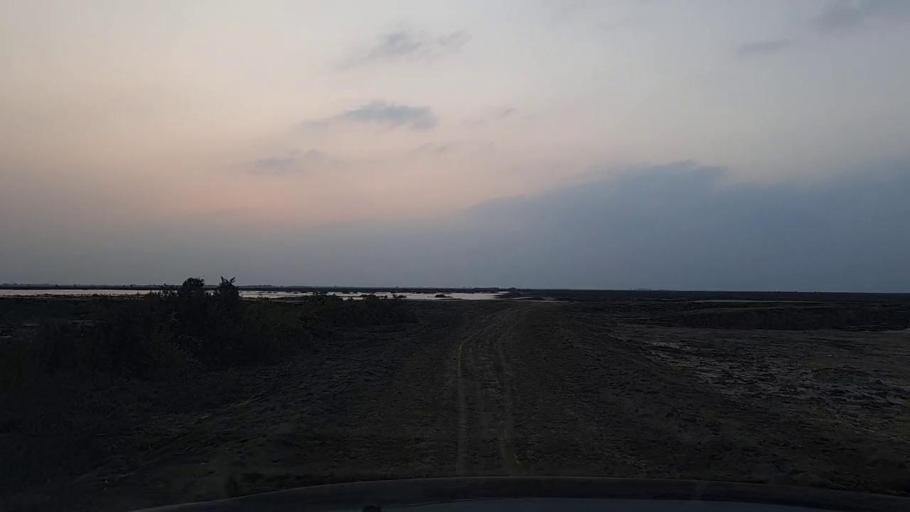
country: PK
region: Sindh
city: Jati
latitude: 24.4947
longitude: 68.3914
